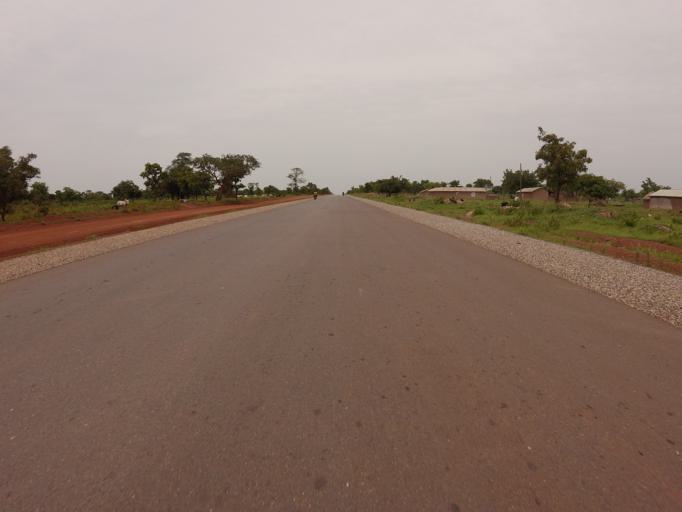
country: GH
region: Northern
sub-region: Yendi
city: Yendi
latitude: 8.9743
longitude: -0.0164
